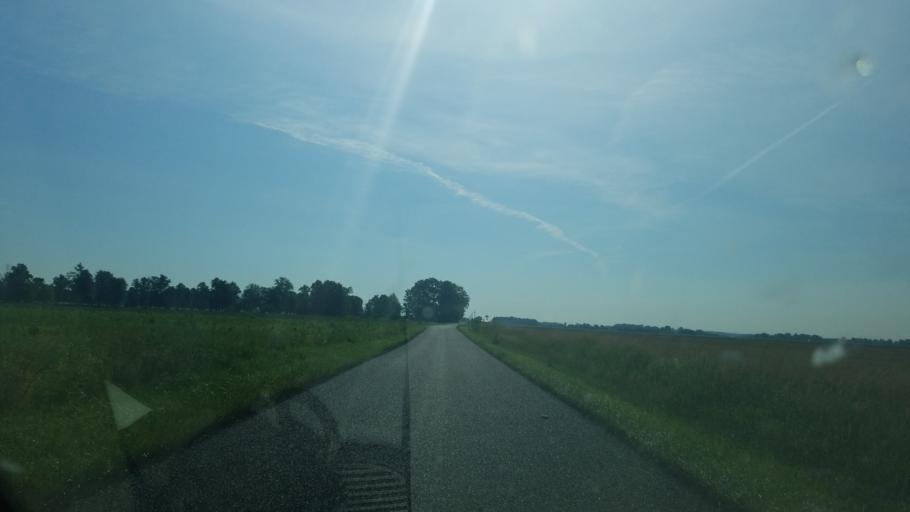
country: US
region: Ohio
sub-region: Hancock County
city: Findlay
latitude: 41.0215
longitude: -83.5371
